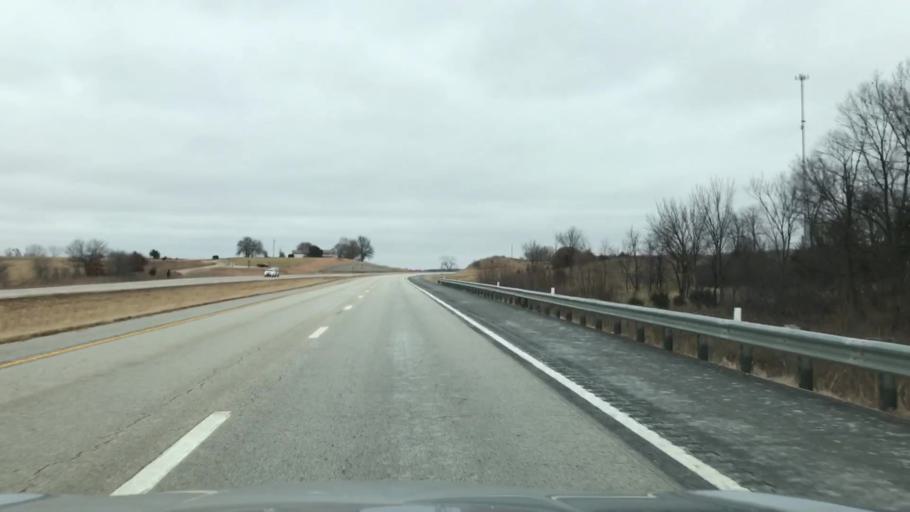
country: US
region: Missouri
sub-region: Caldwell County
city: Hamilton
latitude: 39.7489
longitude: -94.0587
